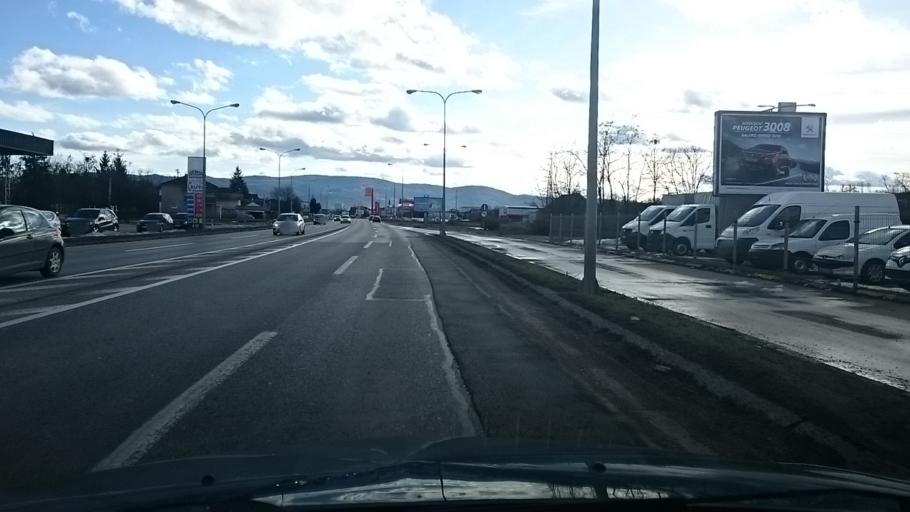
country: BA
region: Republika Srpska
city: Banja Luka
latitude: 44.8089
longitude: 17.1981
